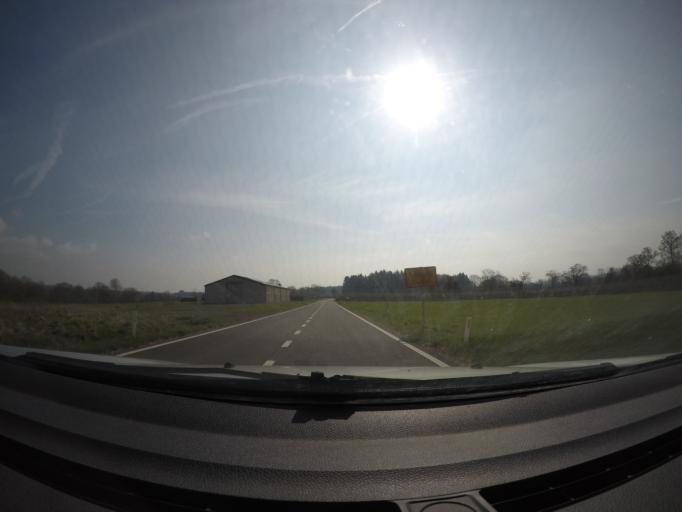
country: BE
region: Wallonia
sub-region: Province du Luxembourg
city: Tintigny
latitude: 49.7185
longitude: 5.4728
